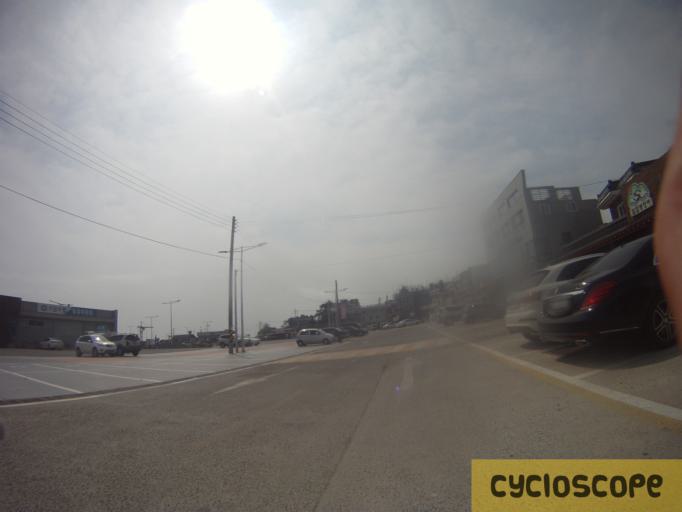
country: KR
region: Busan
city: Kijang
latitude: 35.2973
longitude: 129.2608
